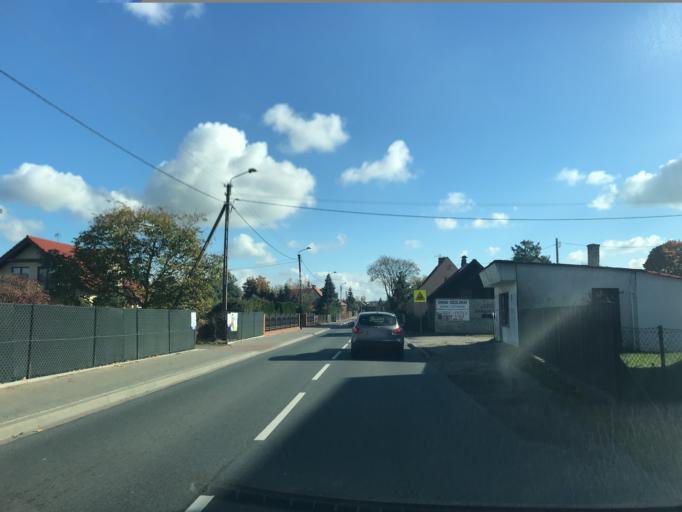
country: PL
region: Warmian-Masurian Voivodeship
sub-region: Powiat ostrodzki
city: Milomlyn
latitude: 53.6663
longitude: 19.8164
